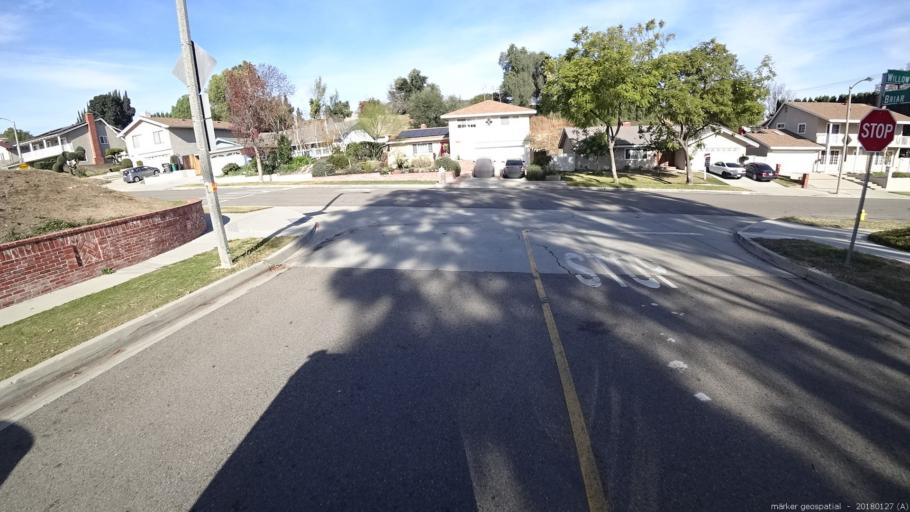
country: US
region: California
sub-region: Los Angeles County
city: Diamond Bar
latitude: 34.0307
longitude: -117.7972
